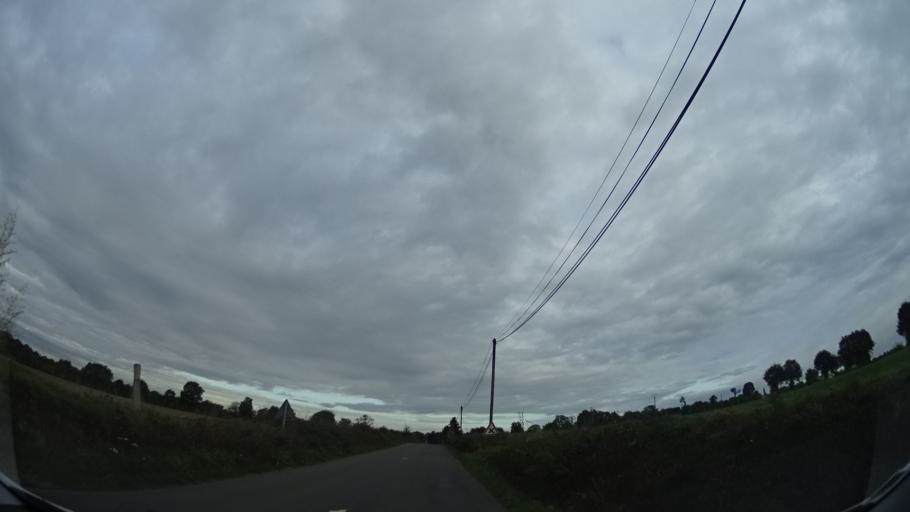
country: FR
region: Brittany
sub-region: Departement d'Ille-et-Vilaine
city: Geveze
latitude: 48.2252
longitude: -1.7860
